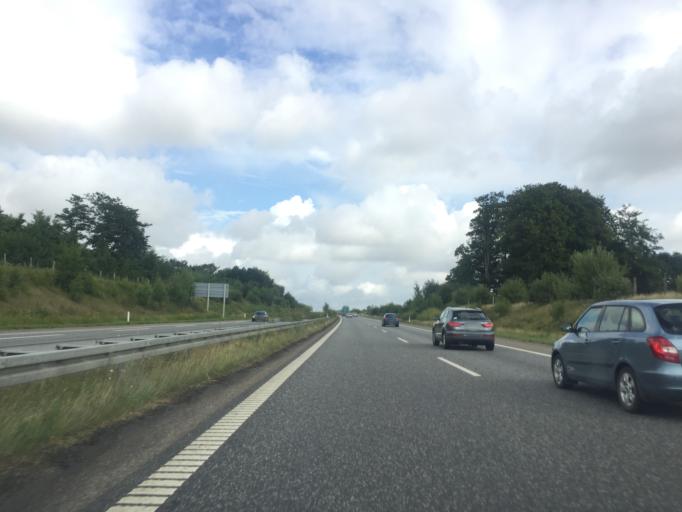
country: DK
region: South Denmark
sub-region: Faaborg-Midtfyn Kommune
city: Ringe
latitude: 55.2605
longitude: 10.4702
